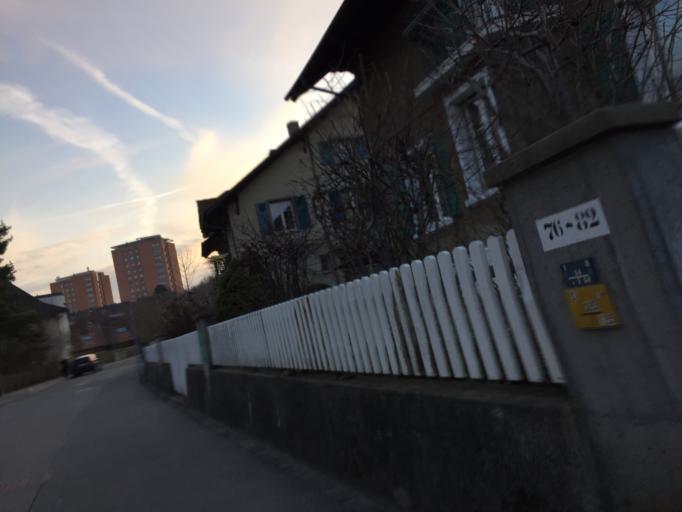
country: CH
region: Bern
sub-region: Bern-Mittelland District
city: Koniz
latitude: 46.9404
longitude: 7.4171
